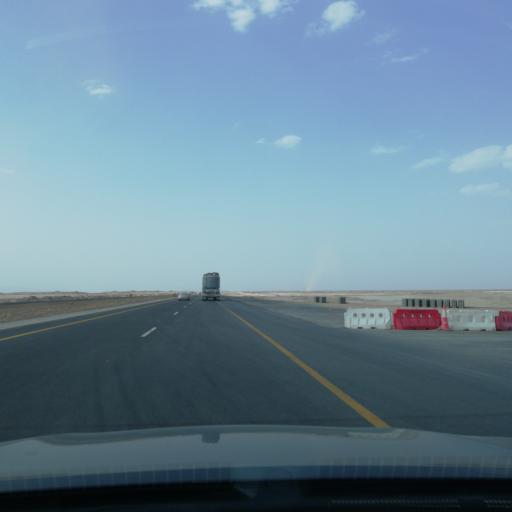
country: OM
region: Muhafazat ad Dakhiliyah
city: Adam
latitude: 22.0663
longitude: 57.5138
